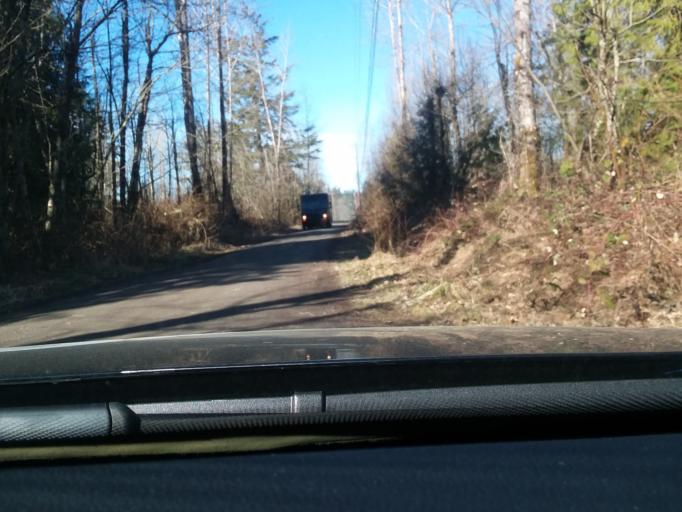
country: US
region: Washington
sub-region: Pierce County
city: Summit
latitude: 47.1341
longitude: -122.3538
